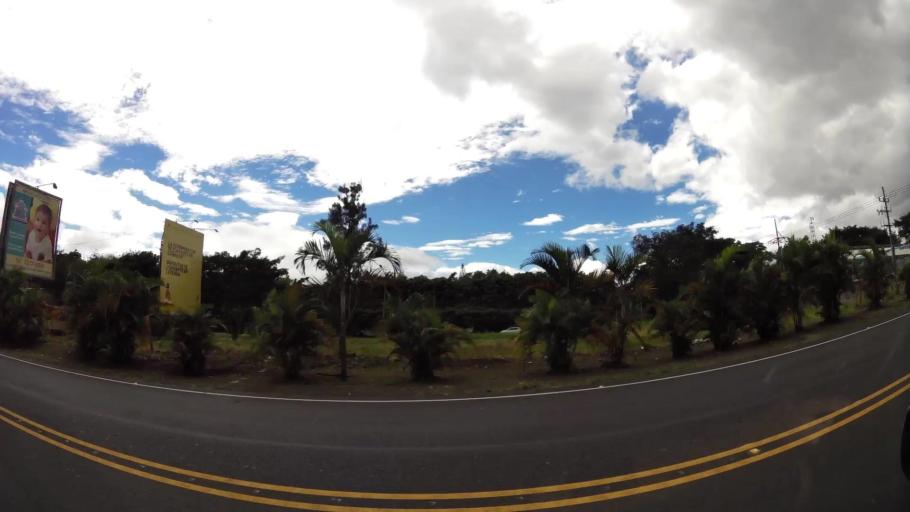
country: CR
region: San Jose
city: Curridabat
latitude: 9.9122
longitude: -84.0220
